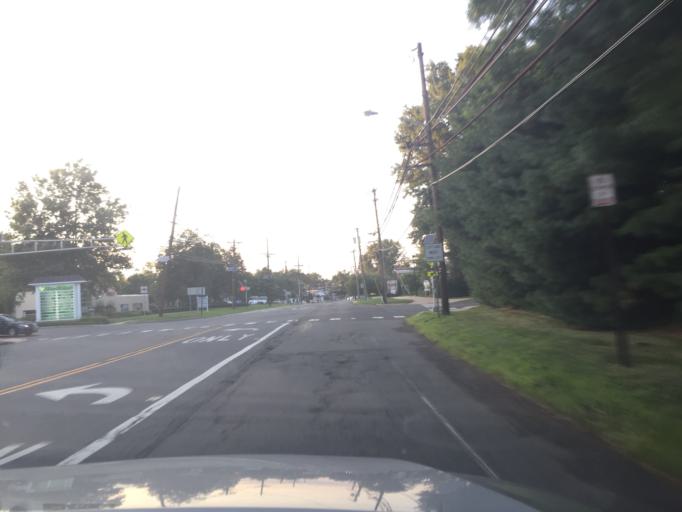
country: US
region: New Jersey
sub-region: Mercer County
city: Princeton Junction
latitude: 40.3129
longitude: -74.6195
